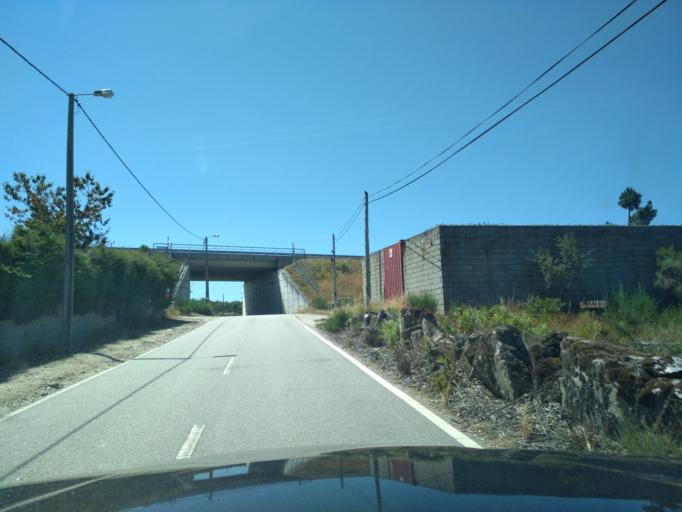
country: PT
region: Vila Real
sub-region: Vila Pouca de Aguiar
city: Vila Pouca de Aguiar
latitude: 41.4963
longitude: -7.6694
